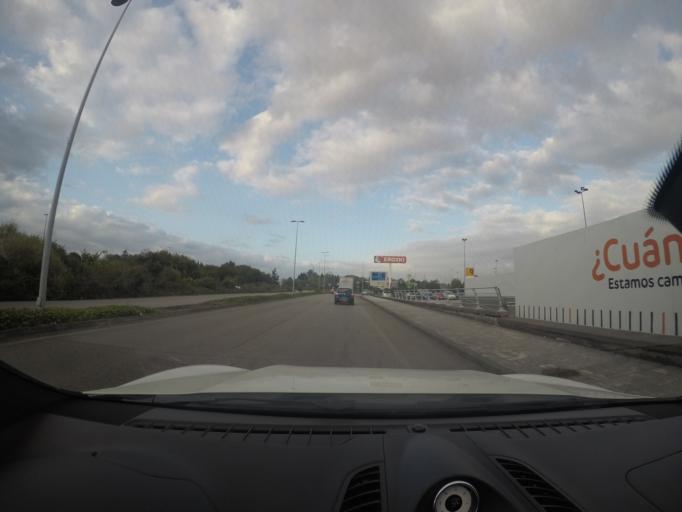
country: ES
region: Asturias
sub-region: Province of Asturias
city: Lugones
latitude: 43.3907
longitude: -5.8051
